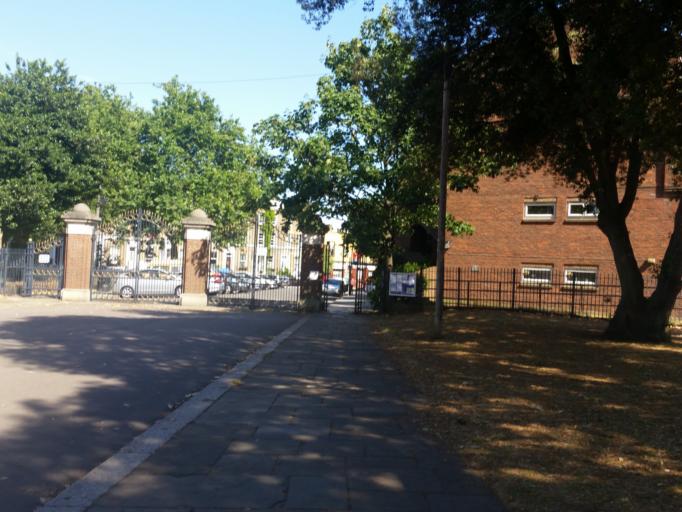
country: GB
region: England
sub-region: Greater London
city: Hackney
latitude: 51.5399
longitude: -0.0289
